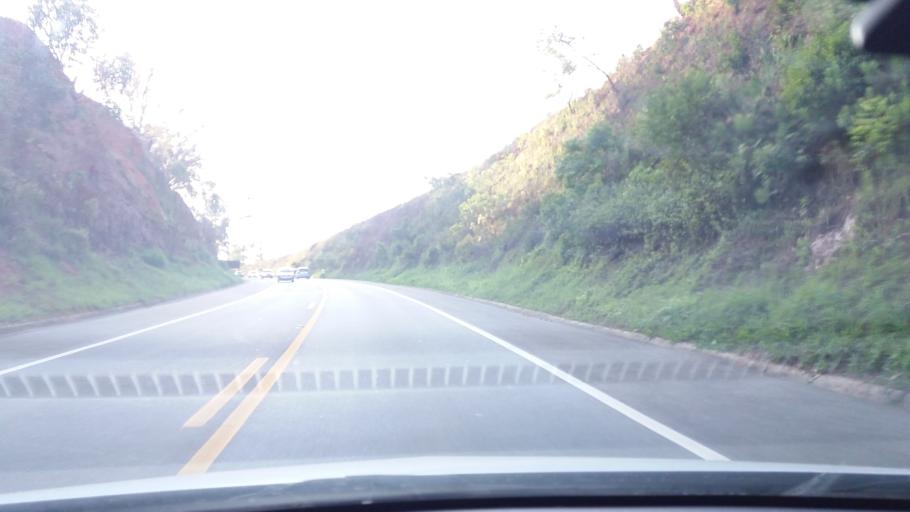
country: BR
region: Sao Paulo
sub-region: Franco Da Rocha
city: Franco da Rocha
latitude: -23.3323
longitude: -46.6793
